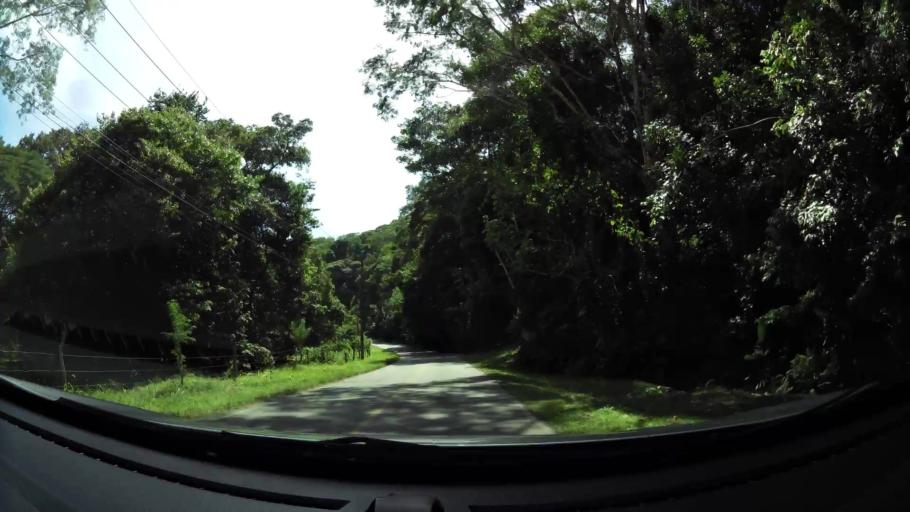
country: CR
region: San Jose
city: San Isidro
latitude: 9.2664
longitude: -83.8639
